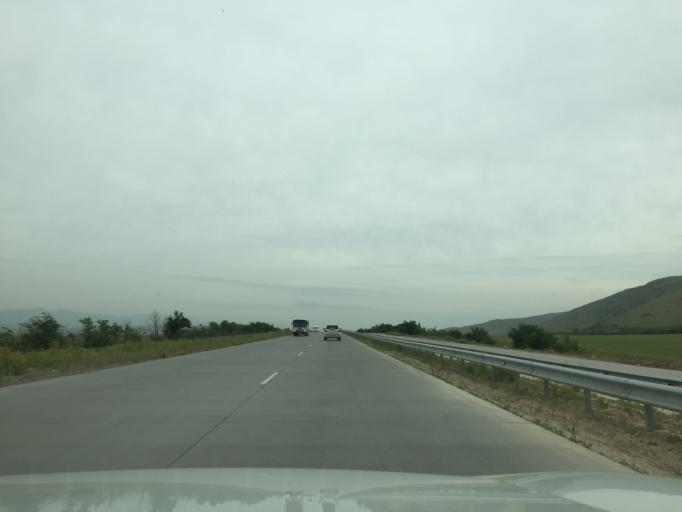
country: KZ
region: Ongtustik Qazaqstan
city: Sastobe
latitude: 42.5425
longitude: 70.0524
